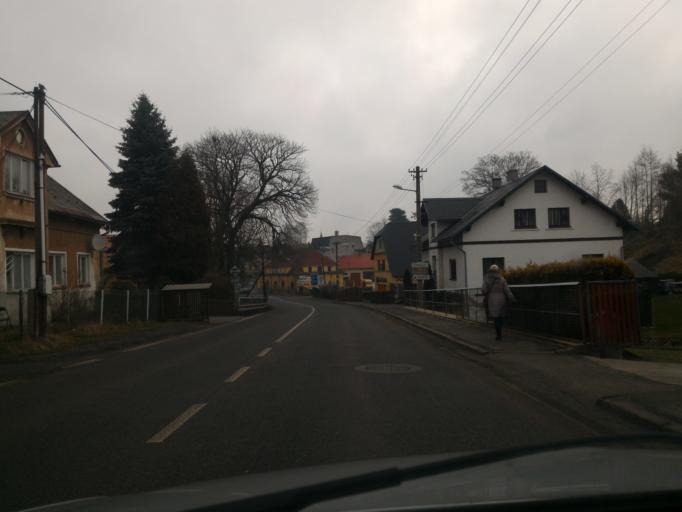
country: CZ
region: Liberecky
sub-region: Okres Liberec
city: Frydlant
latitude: 50.9198
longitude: 15.0709
